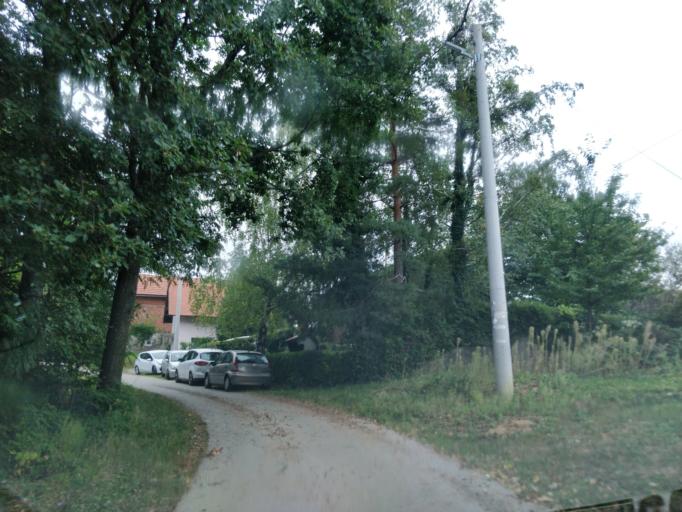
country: HR
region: Krapinsko-Zagorska
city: Oroslavje
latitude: 45.9368
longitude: 15.9182
